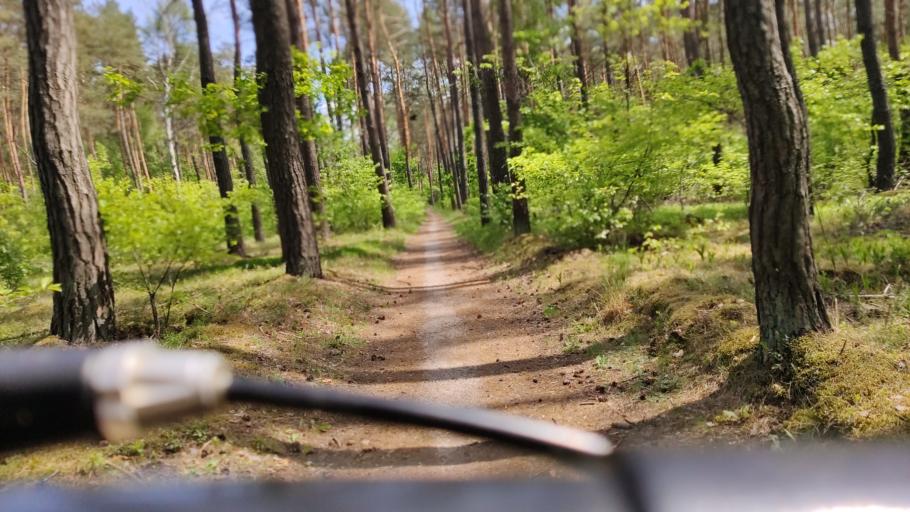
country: PL
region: Kujawsko-Pomorskie
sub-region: Wloclawek
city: Wloclawek
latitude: 52.6326
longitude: 19.1316
